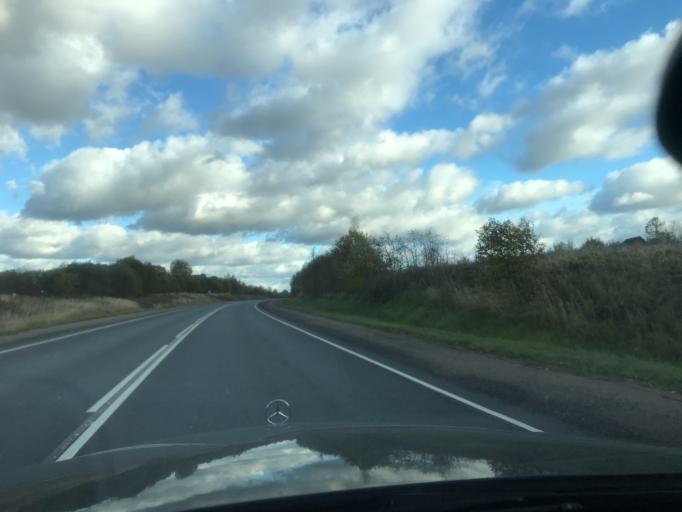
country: RU
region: Pskov
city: Novosokol'niki
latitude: 56.3296
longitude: 30.0897
